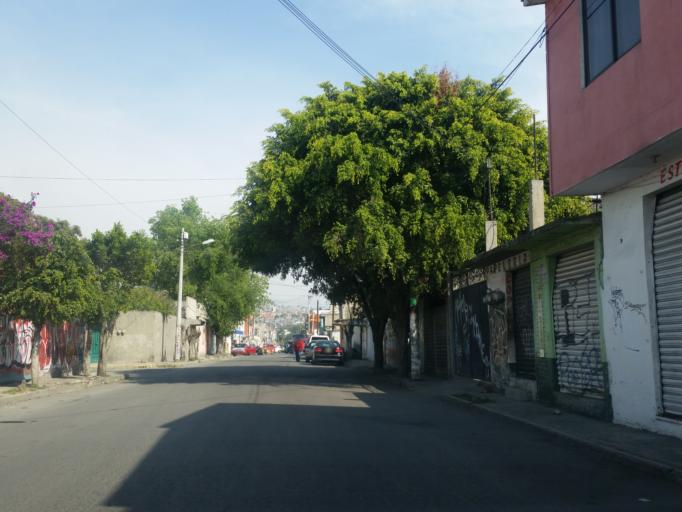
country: MX
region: Mexico
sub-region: La Paz
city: San Isidro
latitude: 19.3241
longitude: -98.9539
